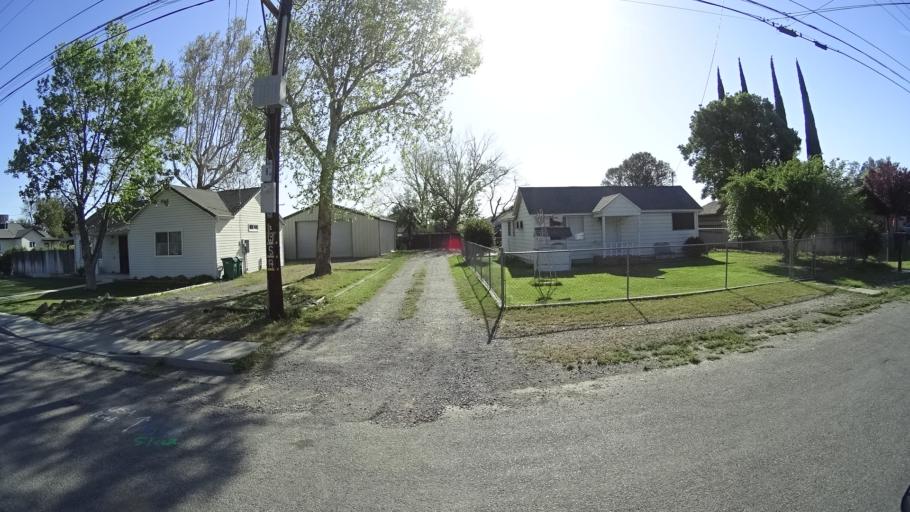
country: US
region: California
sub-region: Glenn County
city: Orland
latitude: 39.7395
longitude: -122.1875
